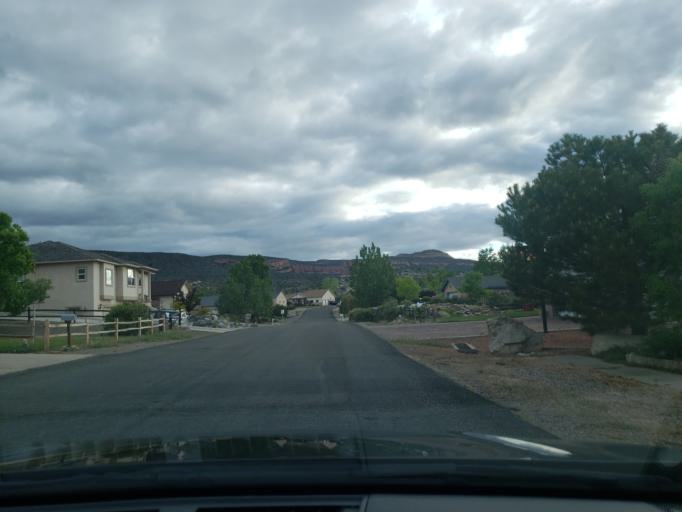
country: US
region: Colorado
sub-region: Mesa County
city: Fruita
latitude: 39.1379
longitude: -108.7428
